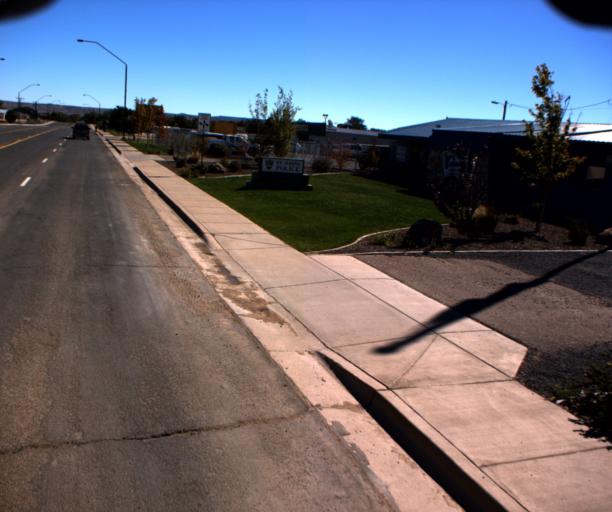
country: US
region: Arizona
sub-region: Apache County
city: Saint Johns
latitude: 34.5064
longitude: -109.3827
